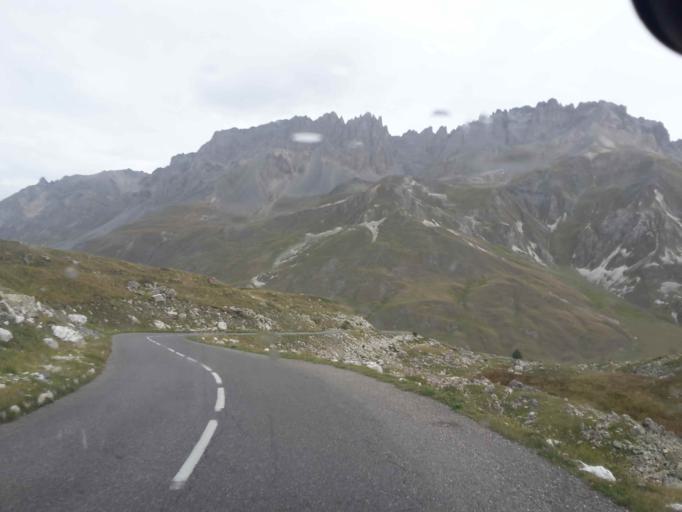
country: FR
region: Rhone-Alpes
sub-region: Departement de la Savoie
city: Valloire
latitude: 45.0836
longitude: 6.4276
